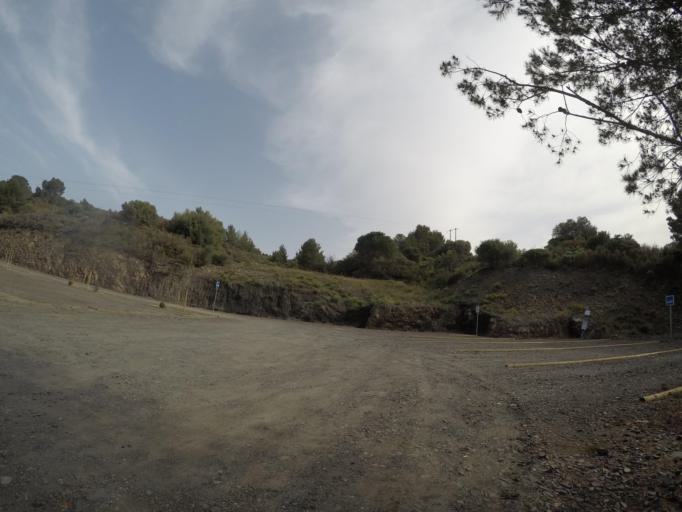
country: FR
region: Languedoc-Roussillon
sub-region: Departement des Pyrenees-Orientales
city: Baixas
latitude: 42.7826
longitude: 2.7792
